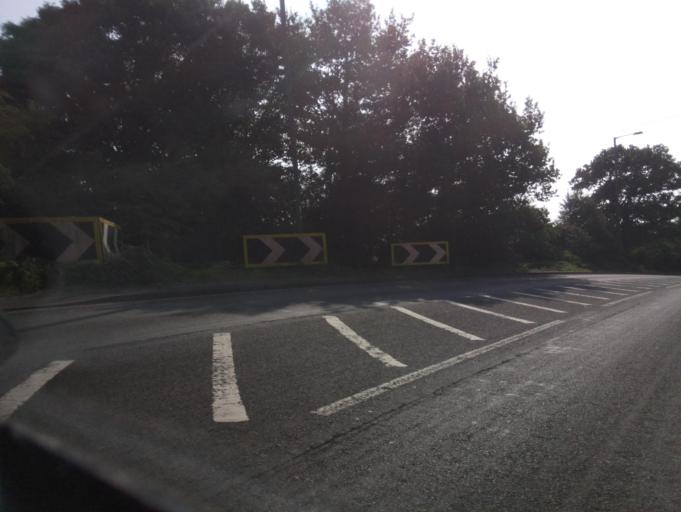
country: GB
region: England
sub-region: Walsall
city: Streetly
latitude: 52.6149
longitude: -1.8859
